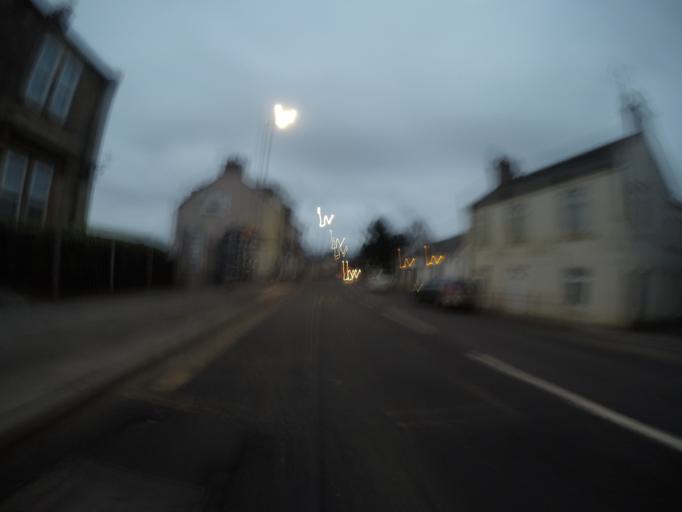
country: GB
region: Scotland
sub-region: North Ayrshire
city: Kilwinning
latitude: 55.6548
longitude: -4.7083
